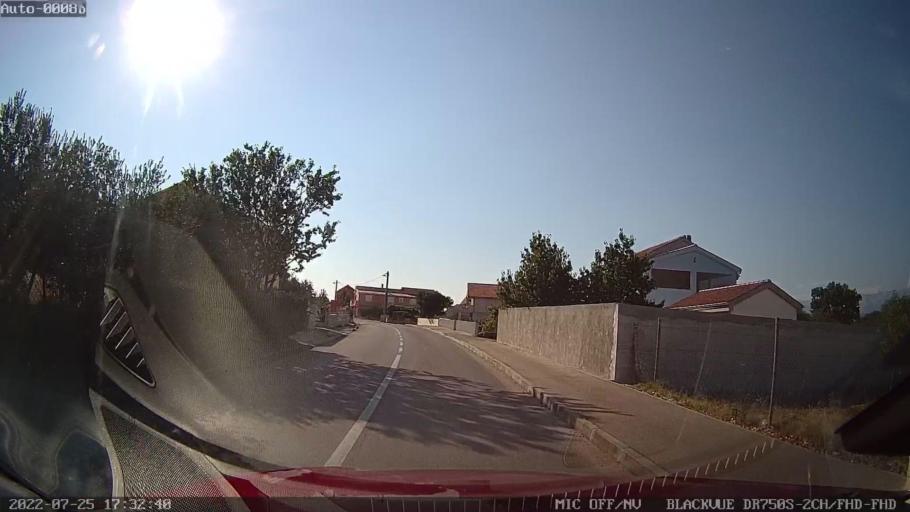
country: HR
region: Zadarska
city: Posedarje
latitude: 44.1778
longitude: 15.4910
